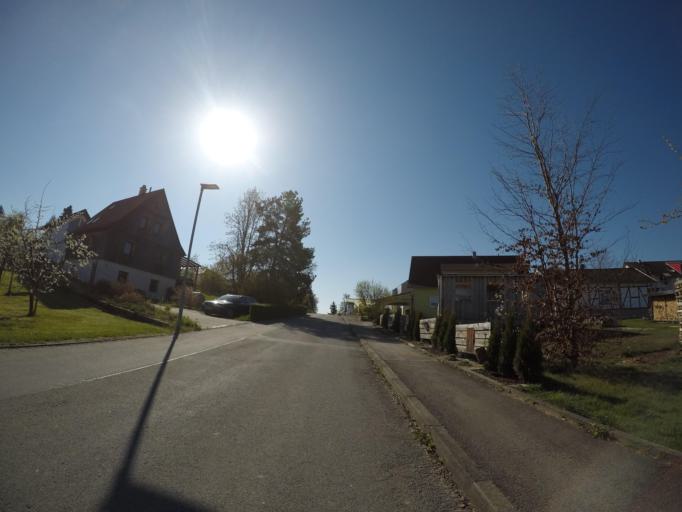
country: DE
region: Baden-Wuerttemberg
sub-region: Tuebingen Region
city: Ebenweiler
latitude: 47.8981
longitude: 9.5155
